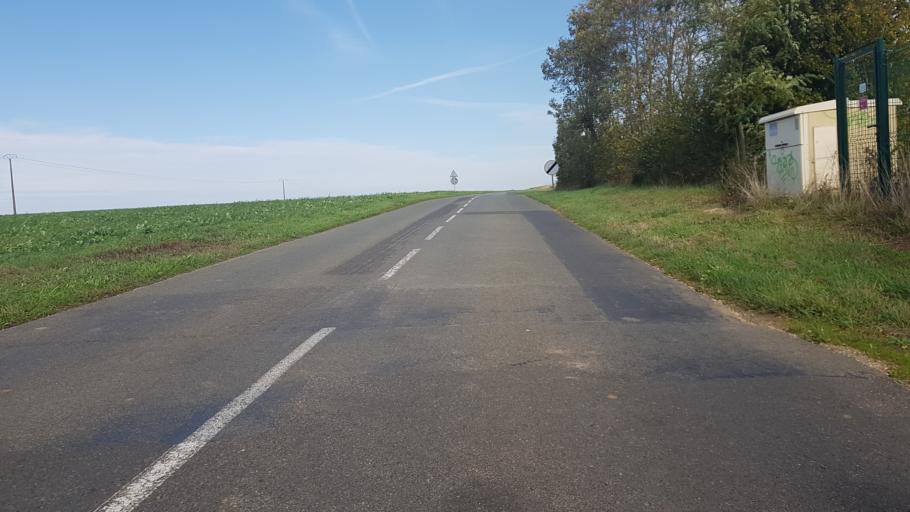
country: FR
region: Poitou-Charentes
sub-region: Departement de la Vienne
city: Chasseneuil-du-Poitou
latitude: 46.6458
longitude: 0.3496
